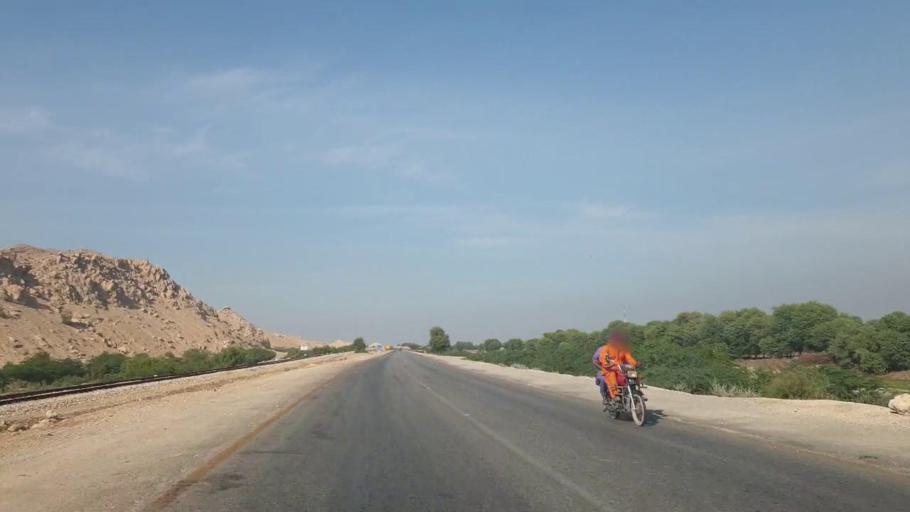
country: PK
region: Sindh
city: Sehwan
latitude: 26.2910
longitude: 67.8943
